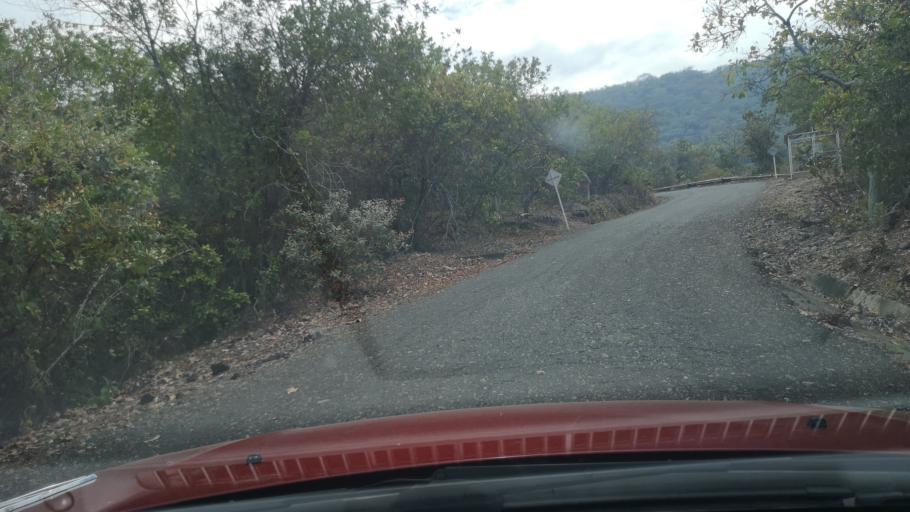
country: CO
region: Huila
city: Neiva
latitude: 2.9574
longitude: -75.3474
